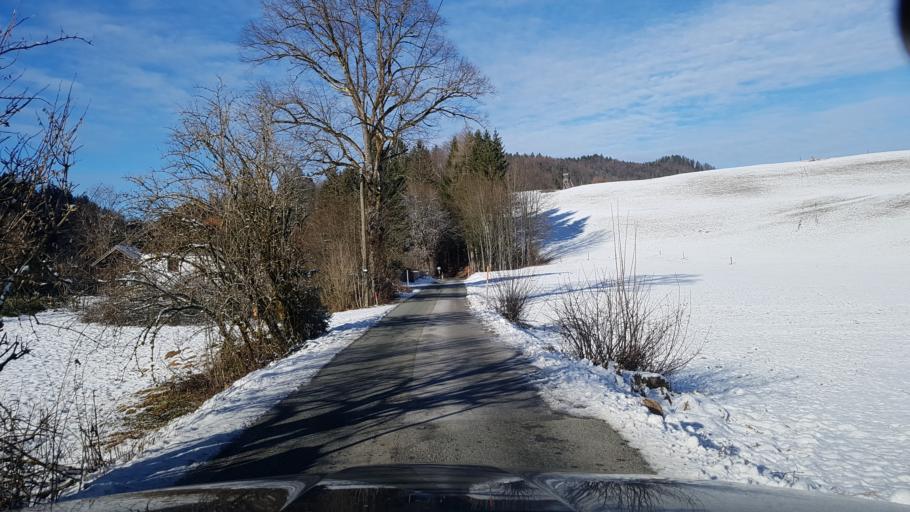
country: AT
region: Salzburg
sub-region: Politischer Bezirk Salzburg-Umgebung
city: Faistenau
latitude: 47.7547
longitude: 13.2391
